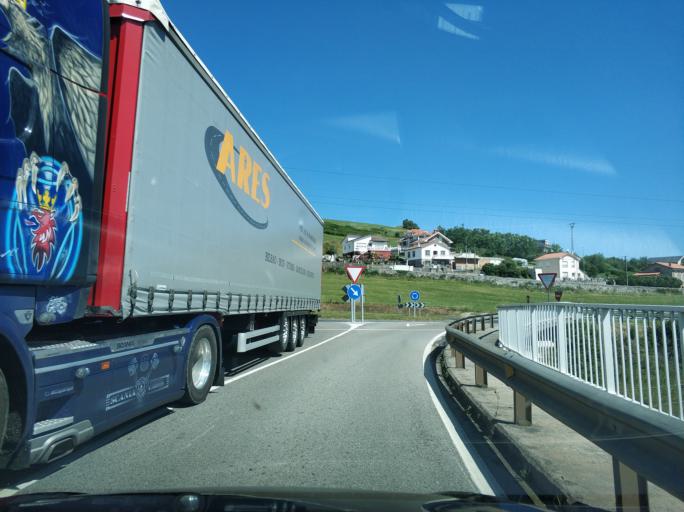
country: ES
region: Cantabria
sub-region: Provincia de Cantabria
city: Camargo
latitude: 43.3907
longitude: -3.8609
